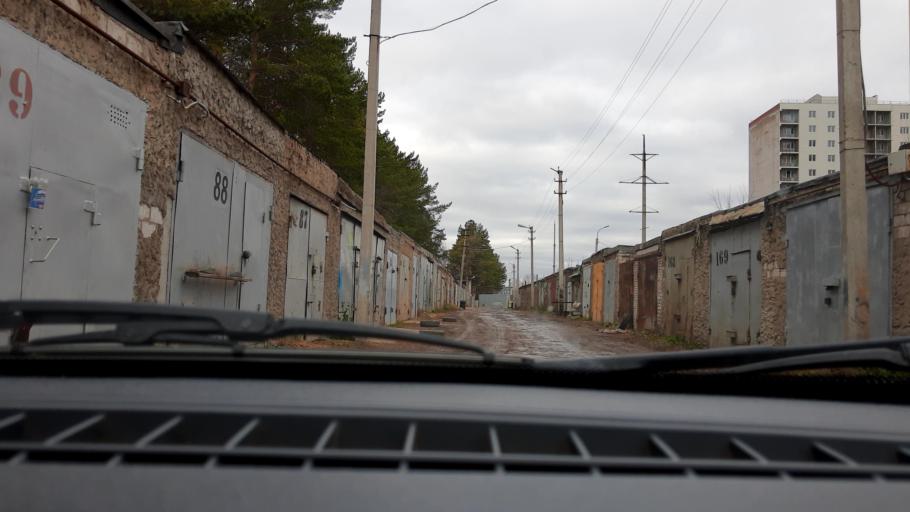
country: RU
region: Bashkortostan
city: Mikhaylovka
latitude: 54.7880
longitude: 55.8700
